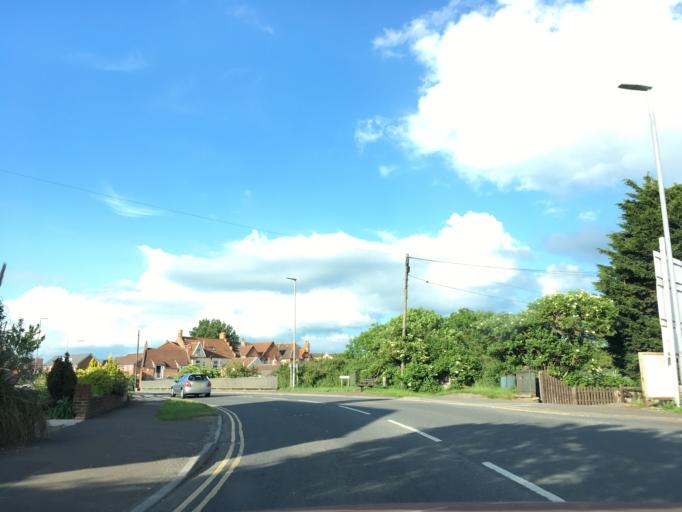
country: GB
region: England
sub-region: Somerset
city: Highbridge
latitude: 51.2185
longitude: -2.9792
